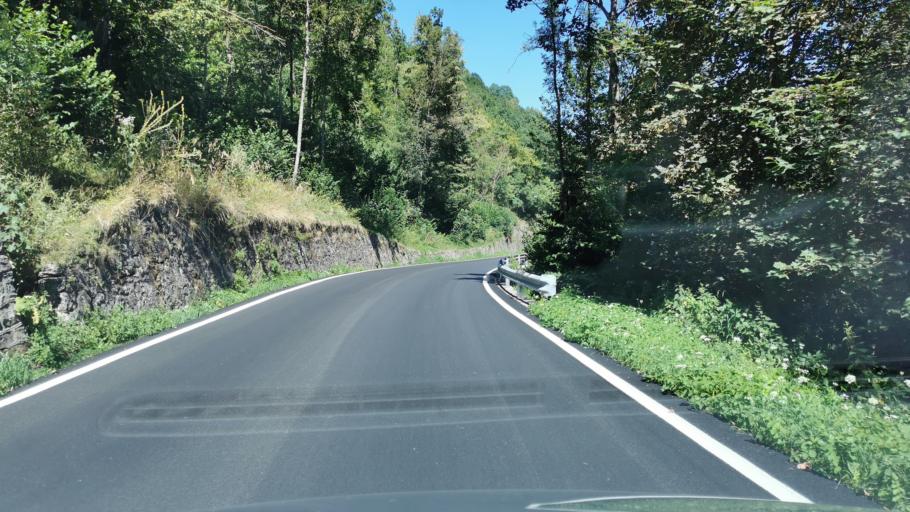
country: IT
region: Piedmont
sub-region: Provincia di Cuneo
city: Entracque
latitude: 44.2509
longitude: 7.3402
